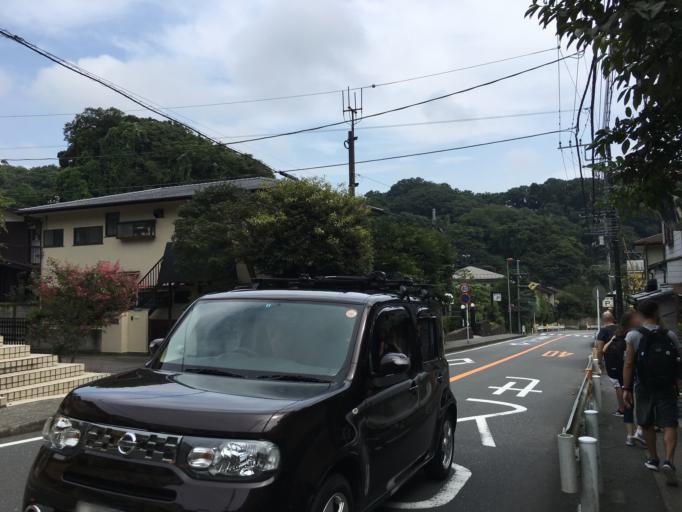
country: JP
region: Kanagawa
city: Kamakura
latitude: 35.3285
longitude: 139.5551
